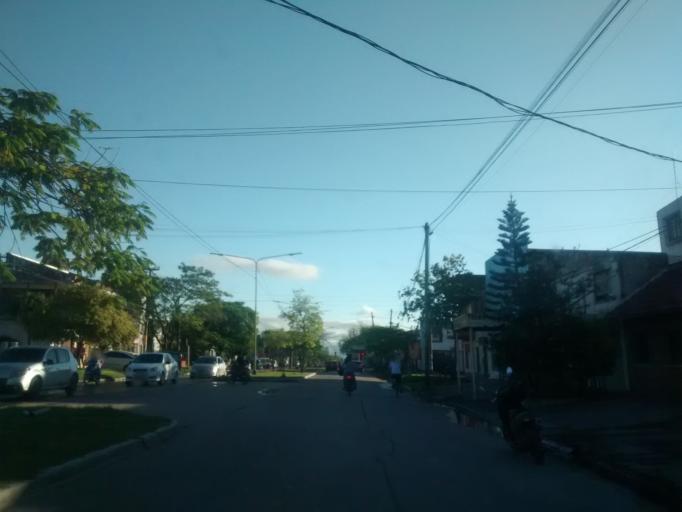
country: AR
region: Chaco
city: Resistencia
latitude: -27.4630
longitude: -58.9997
